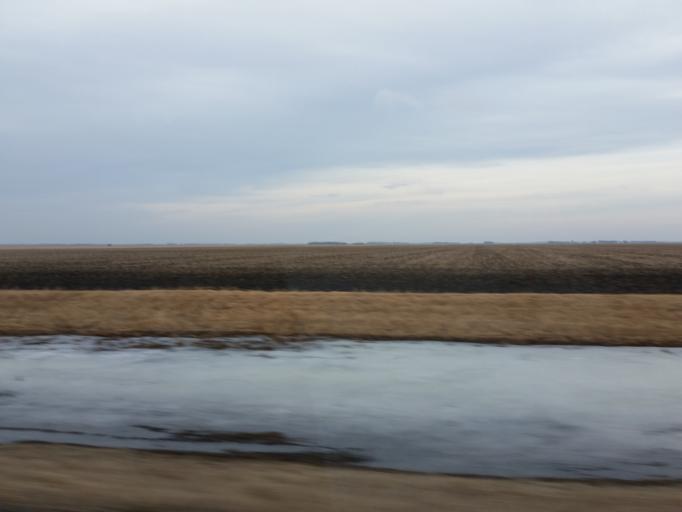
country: US
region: North Dakota
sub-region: Traill County
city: Hillsboro
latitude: 47.2584
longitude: -97.2177
